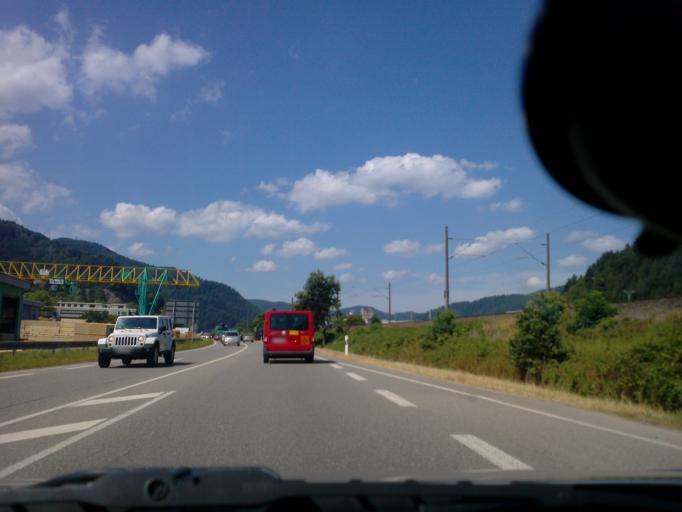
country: DE
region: Baden-Wuerttemberg
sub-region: Freiburg Region
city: Hausach
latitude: 48.2842
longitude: 8.1460
